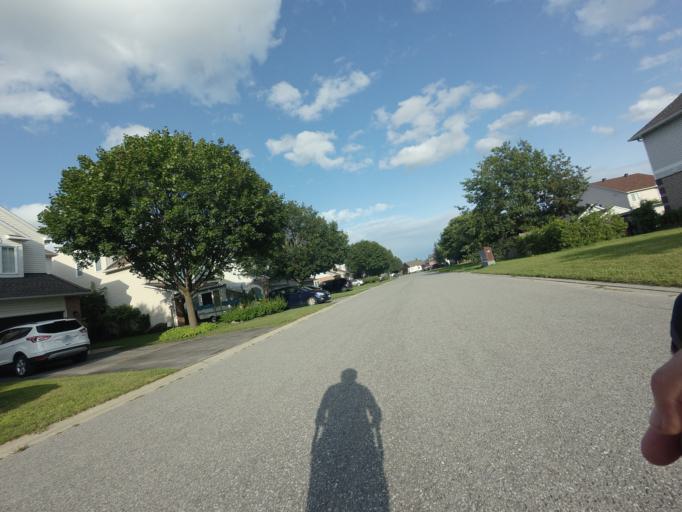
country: CA
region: Ontario
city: Bells Corners
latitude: 45.2876
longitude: -75.7215
